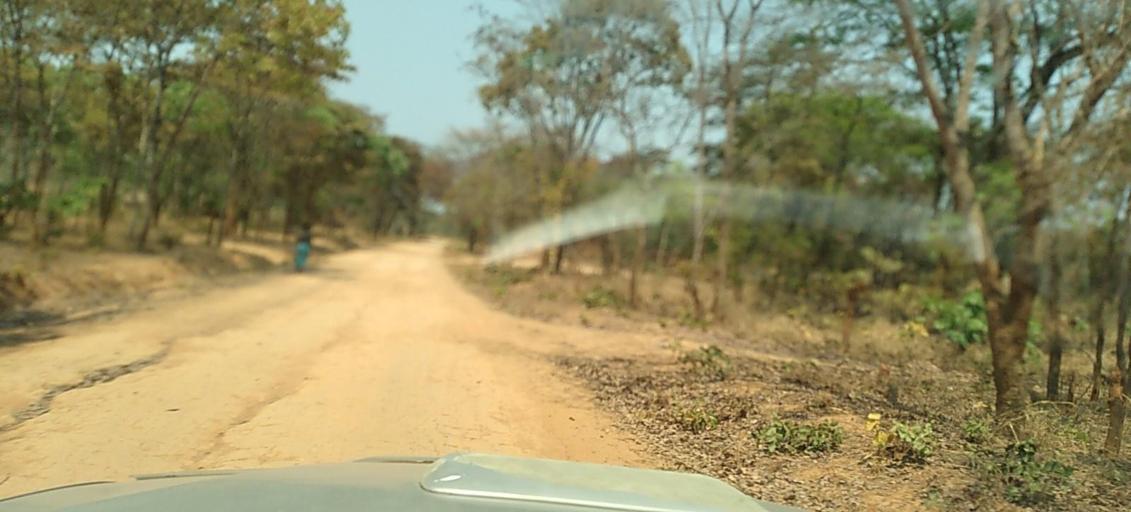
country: ZM
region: North-Western
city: Kasempa
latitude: -13.6664
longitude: 26.2857
